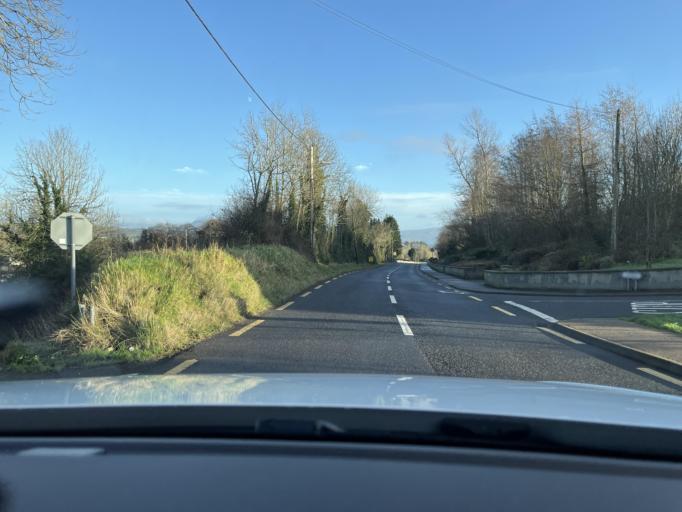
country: IE
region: Connaught
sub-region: County Leitrim
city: Manorhamilton
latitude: 54.1694
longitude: -8.1423
